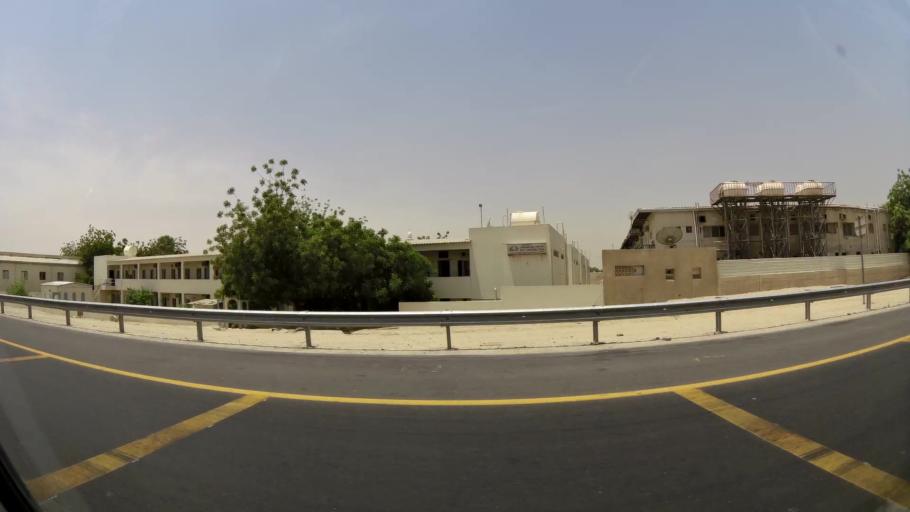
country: AE
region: Ash Shariqah
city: Sharjah
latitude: 25.2760
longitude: 55.4282
